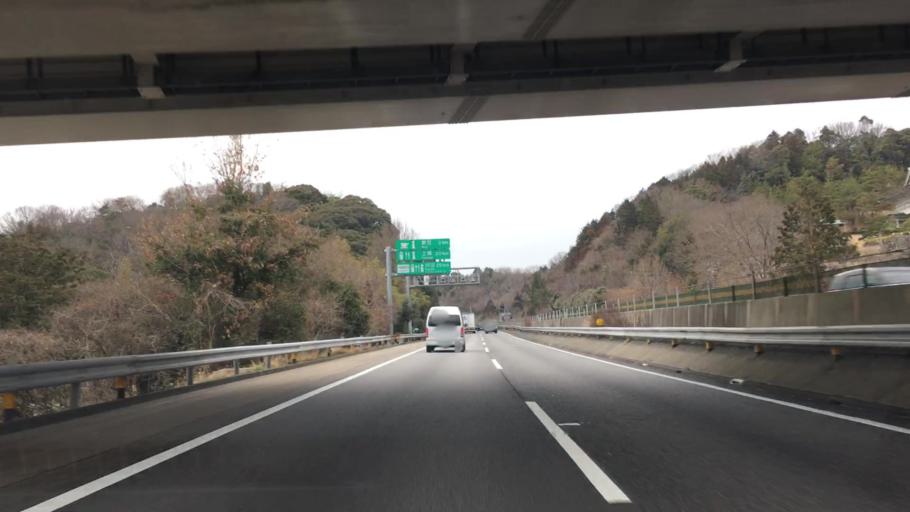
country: JP
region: Aichi
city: Gamagori
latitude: 34.8976
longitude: 137.2568
